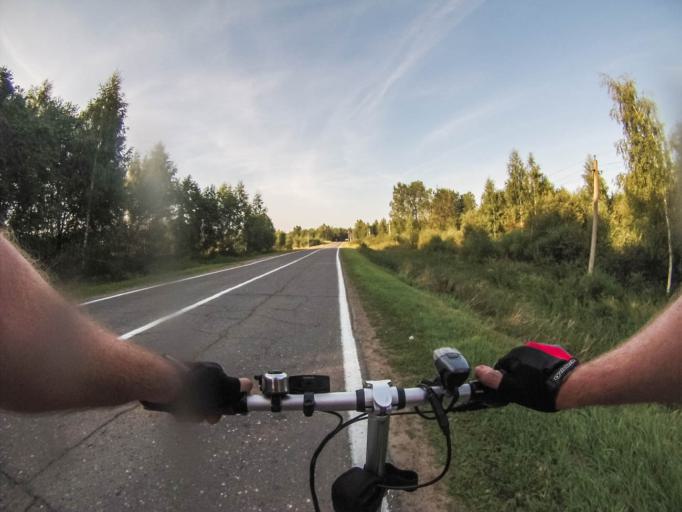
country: RU
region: Jaroslavl
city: Myshkin
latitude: 57.7525
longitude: 38.4384
